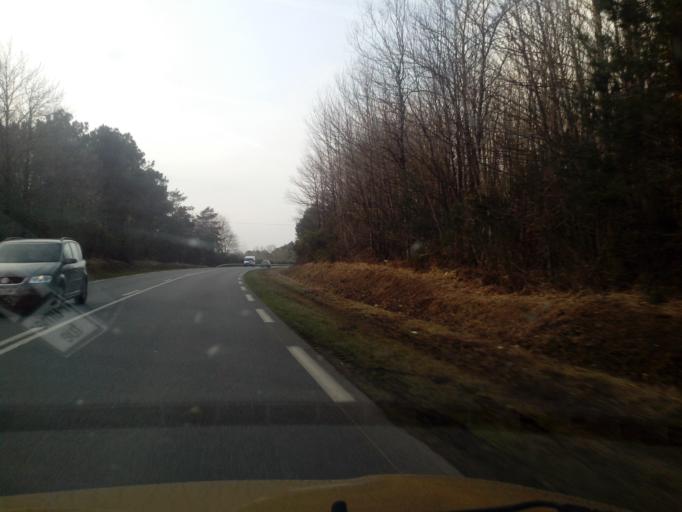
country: FR
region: Brittany
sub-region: Departement du Morbihan
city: Molac
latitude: 47.7671
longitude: -2.4510
